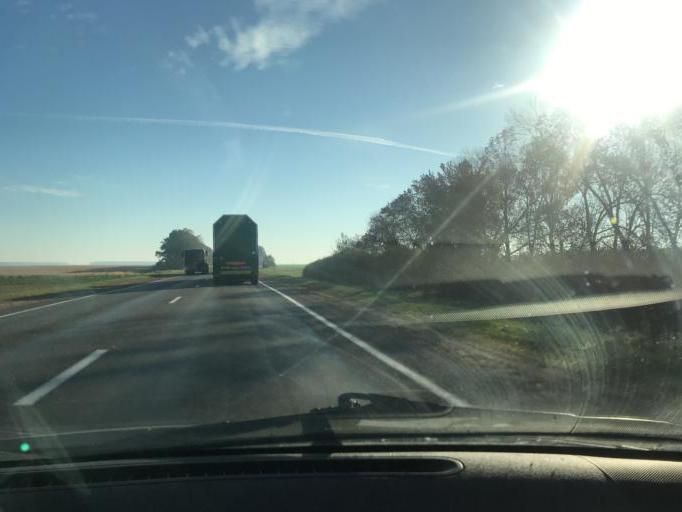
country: BY
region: Brest
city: Ivanava
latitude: 52.1490
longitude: 25.4046
